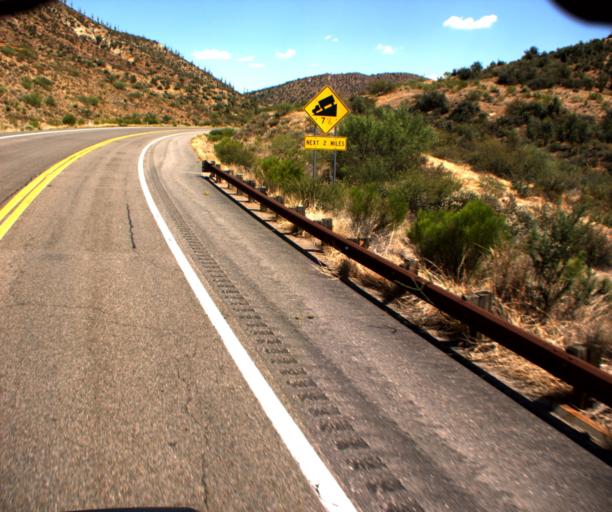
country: US
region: Arizona
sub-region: Gila County
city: Claypool
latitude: 33.5252
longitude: -110.8937
